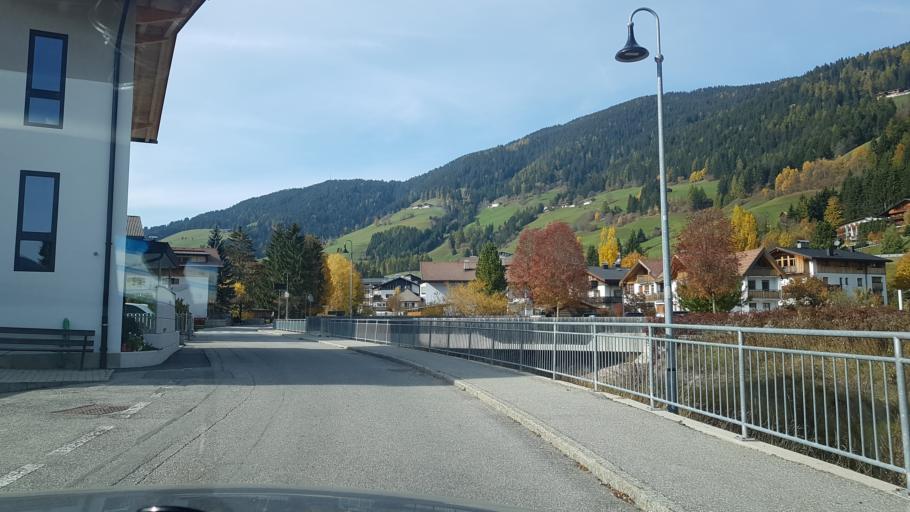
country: IT
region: Trentino-Alto Adige
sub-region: Bolzano
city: San Candido
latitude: 46.7341
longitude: 12.2878
